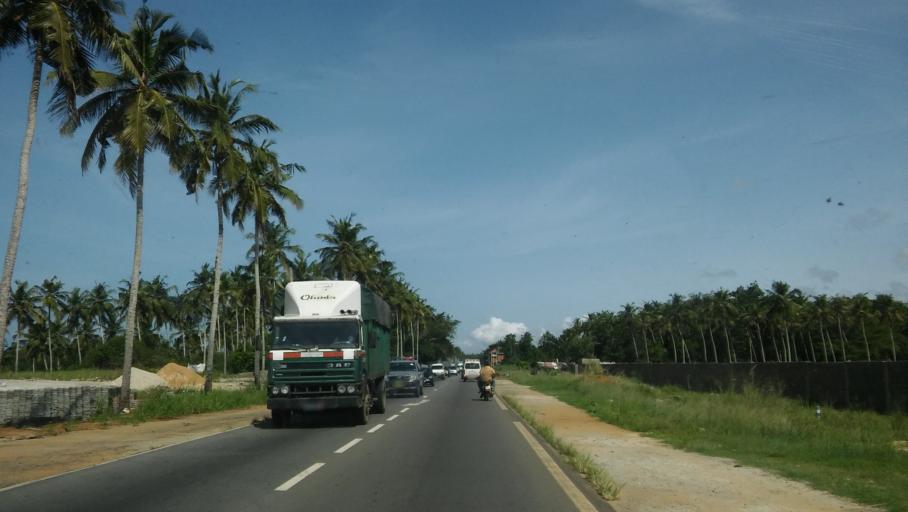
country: CI
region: Sud-Comoe
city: Grand-Bassam
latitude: 5.2154
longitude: -3.7925
